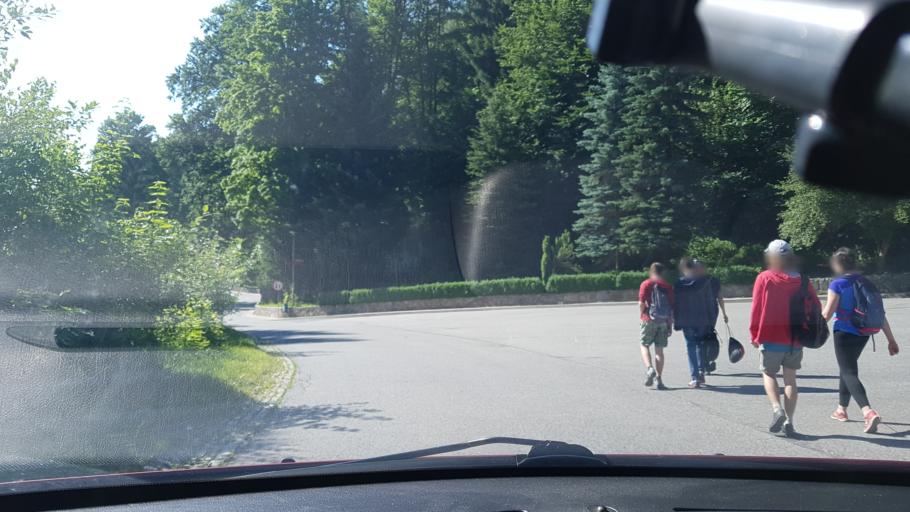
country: PL
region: Lower Silesian Voivodeship
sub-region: Powiat klodzki
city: Stronie Slaskie
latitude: 50.2279
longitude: 16.7678
